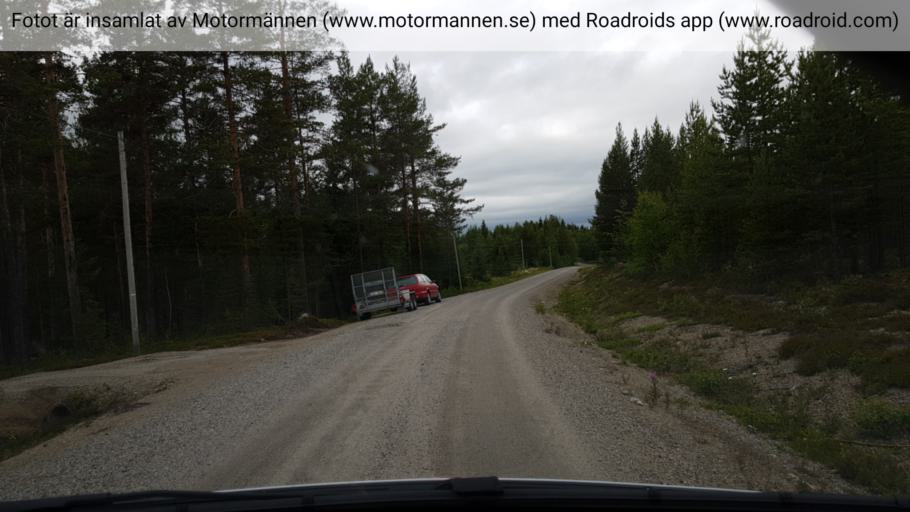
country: SE
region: Vaesterbotten
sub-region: Lycksele Kommun
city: Lycksele
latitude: 64.5716
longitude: 19.0154
